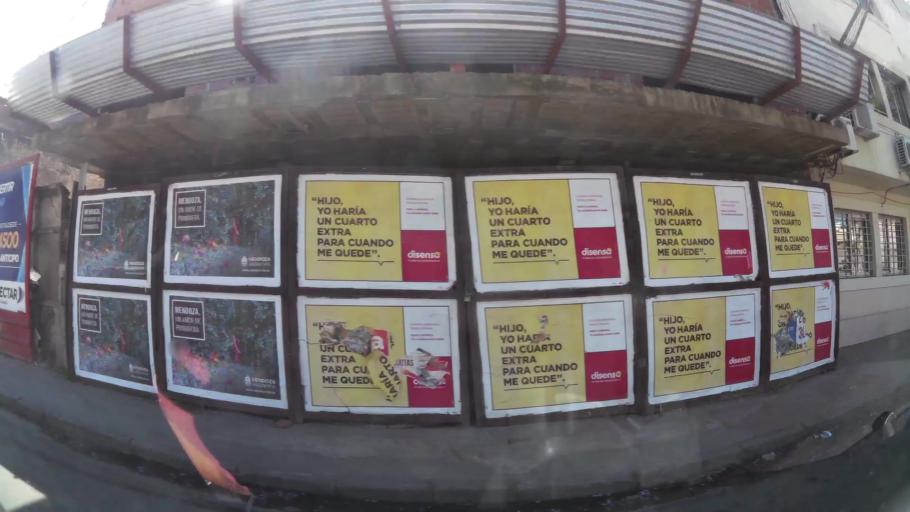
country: AR
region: Cordoba
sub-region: Departamento de Capital
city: Cordoba
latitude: -31.4139
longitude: -64.1981
